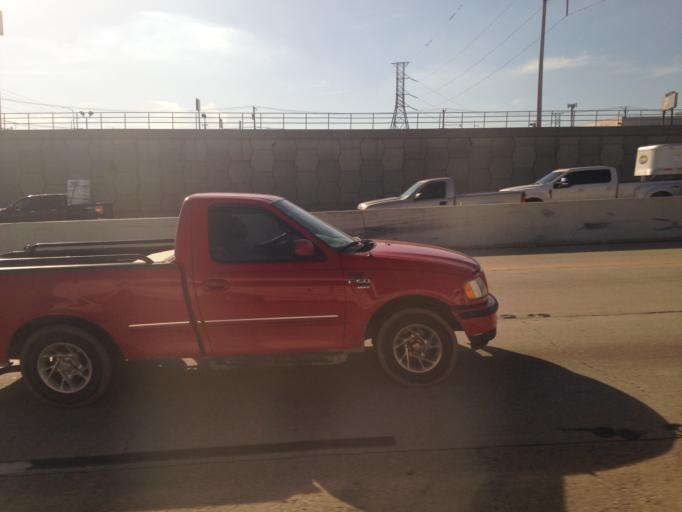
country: US
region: Texas
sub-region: Tarrant County
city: Fort Worth
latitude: 32.7364
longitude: -97.3203
